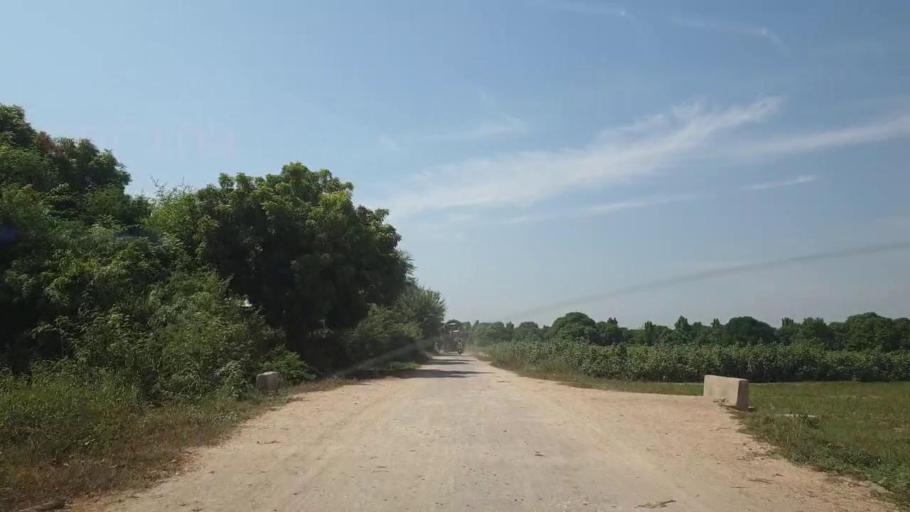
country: PK
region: Sindh
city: Tando Allahyar
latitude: 25.3993
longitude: 68.6436
